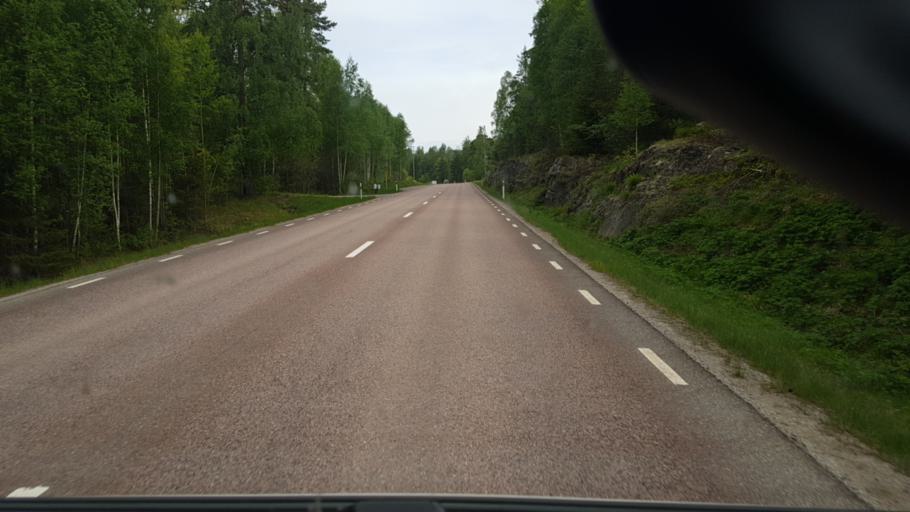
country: SE
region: Vaermland
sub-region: Arvika Kommun
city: Arvika
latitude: 59.6119
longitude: 12.6192
